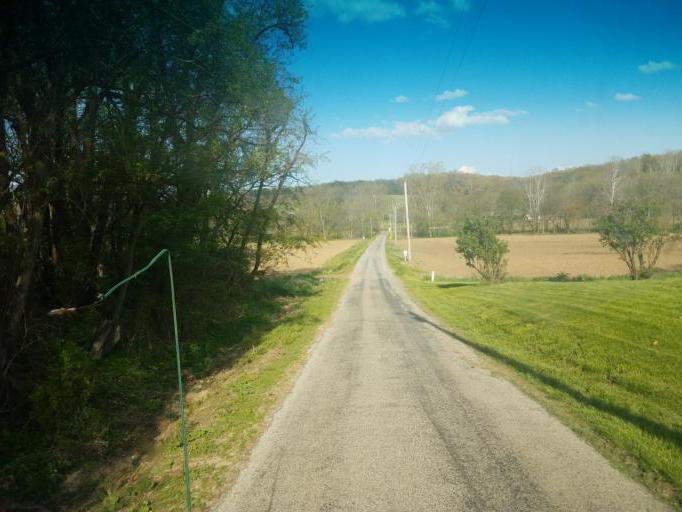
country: US
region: Ohio
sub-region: Wayne County
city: Shreve
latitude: 40.6861
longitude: -81.9470
